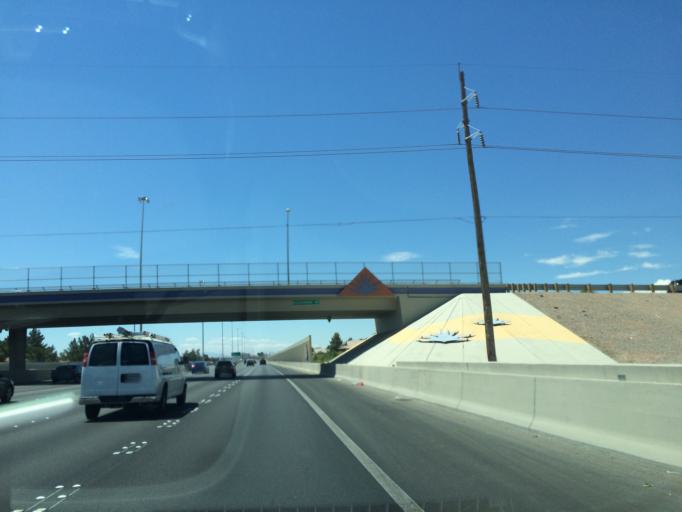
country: US
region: Nevada
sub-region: Clark County
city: Las Vegas
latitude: 36.2336
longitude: -115.2472
